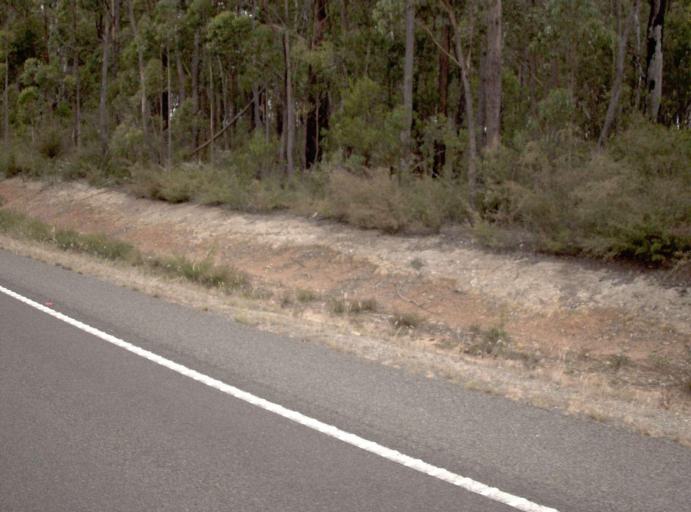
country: AU
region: Victoria
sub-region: East Gippsland
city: Lakes Entrance
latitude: -37.7213
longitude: 147.9565
